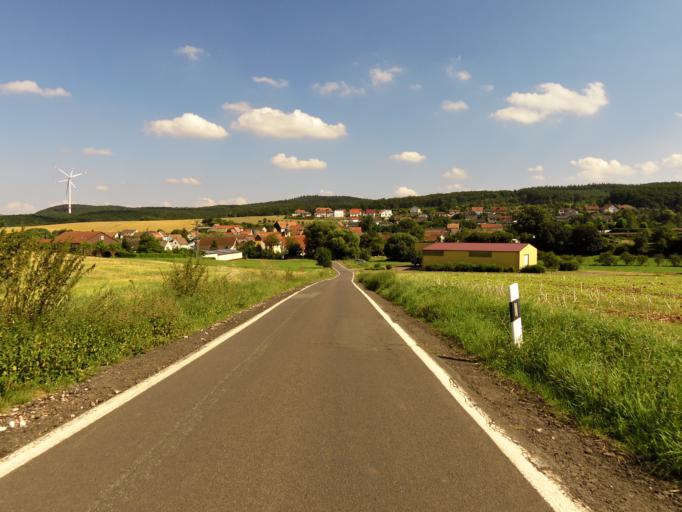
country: DE
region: Rheinland-Pfalz
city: Breunigweiler
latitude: 49.5699
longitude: 7.9591
